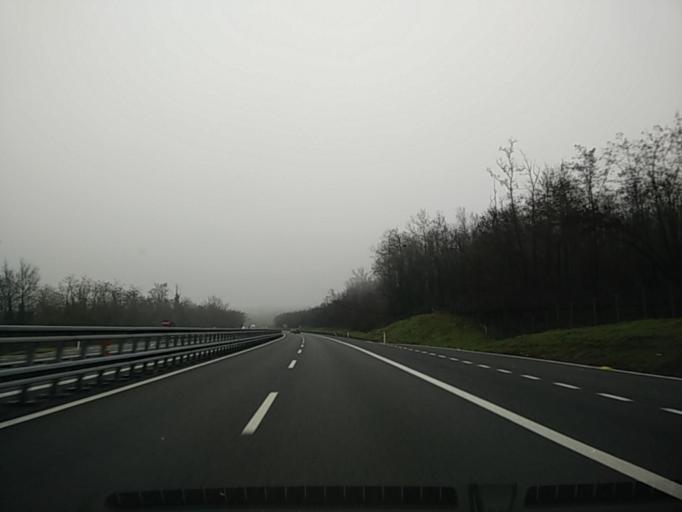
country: IT
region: Piedmont
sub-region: Provincia di Asti
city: Refrancore
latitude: 44.9063
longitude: 8.3383
